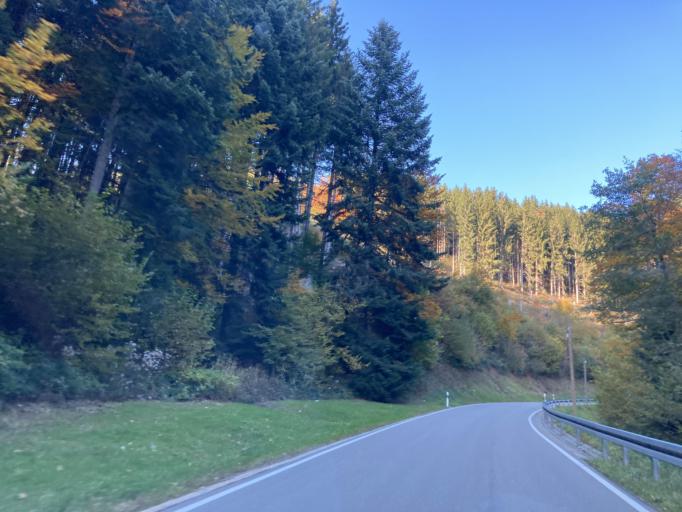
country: DE
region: Baden-Wuerttemberg
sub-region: Freiburg Region
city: Sankt Margen
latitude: 47.9723
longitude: 8.0894
